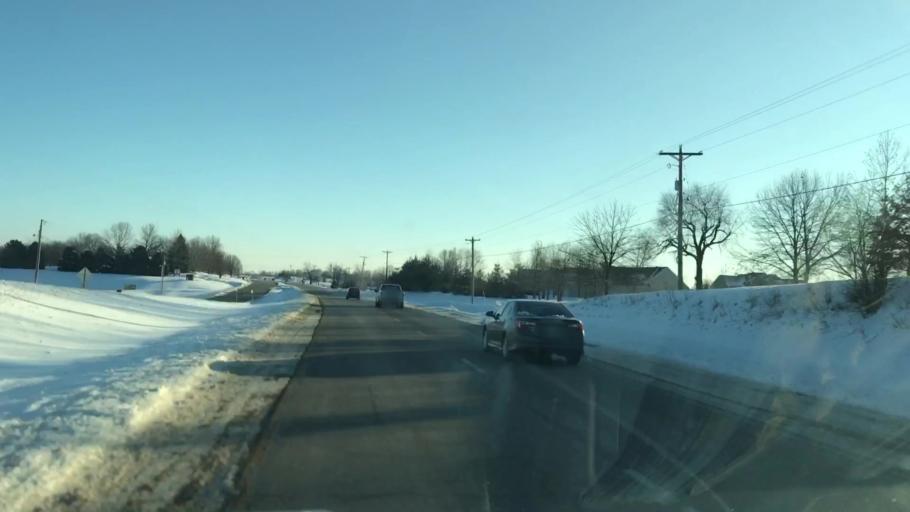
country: US
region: Missouri
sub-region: Andrew County
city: Country Club Village
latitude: 39.8776
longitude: -94.8092
